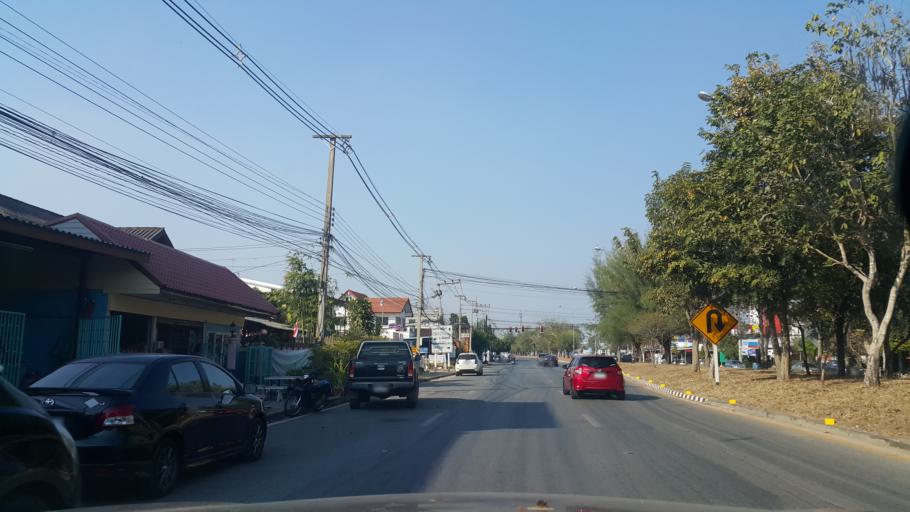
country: TH
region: Nakhon Ratchasima
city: Phimai
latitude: 15.2277
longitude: 102.4942
